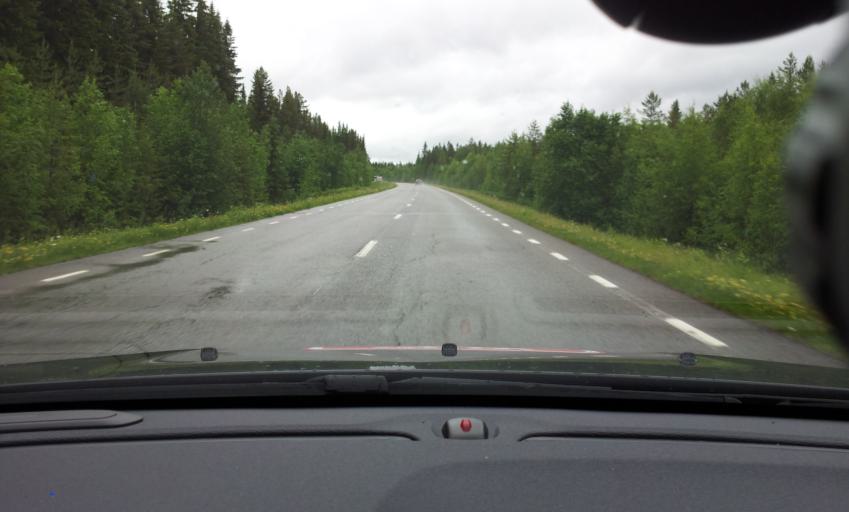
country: SE
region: Jaemtland
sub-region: OEstersunds Kommun
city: Lit
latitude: 63.6022
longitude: 14.6644
